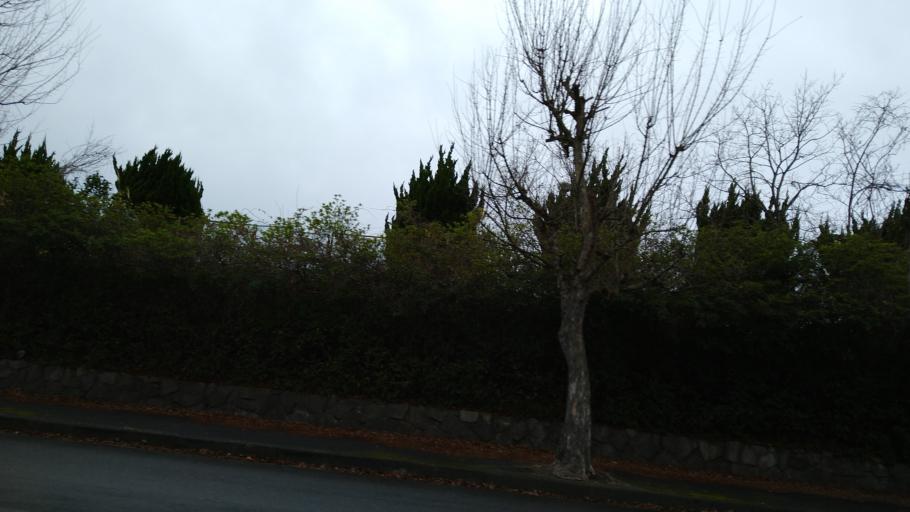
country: JP
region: Kyoto
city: Fukuchiyama
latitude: 35.2885
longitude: 135.1583
